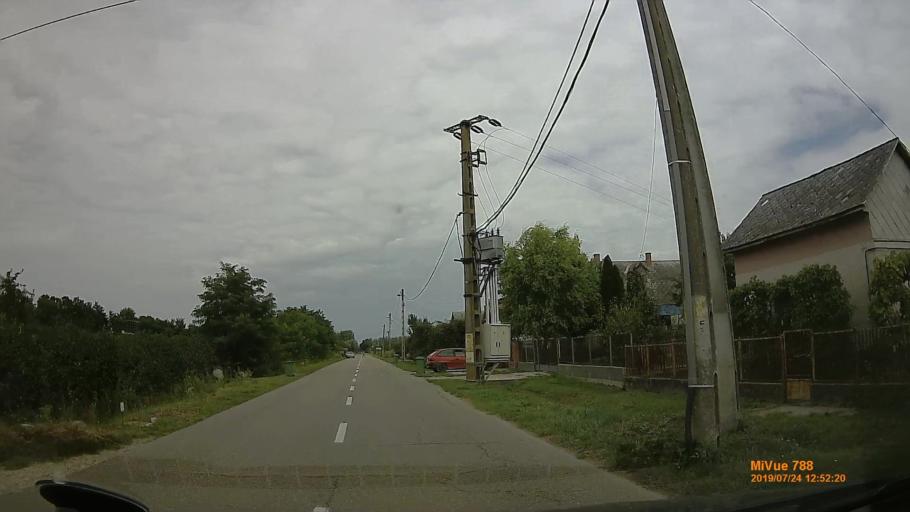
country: HU
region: Szabolcs-Szatmar-Bereg
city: Aranyosapati
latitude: 48.1971
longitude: 22.2984
